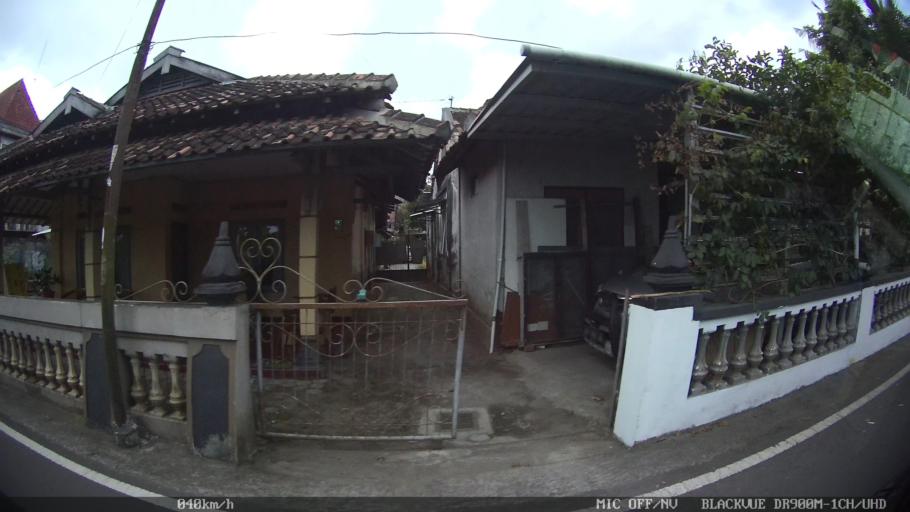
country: ID
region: Daerah Istimewa Yogyakarta
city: Gamping Lor
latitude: -7.7835
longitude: 110.3322
